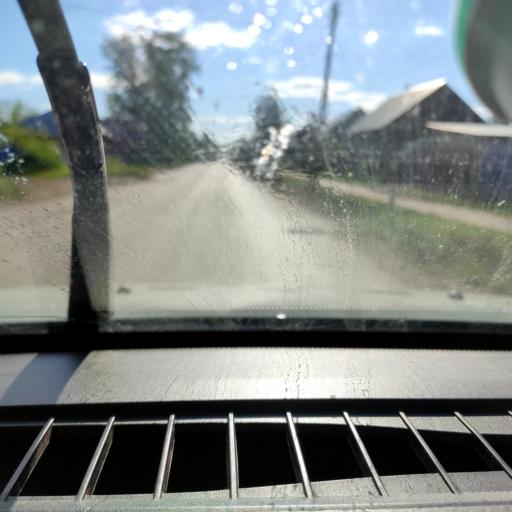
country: RU
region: Perm
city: Ocher
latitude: 57.8827
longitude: 54.7306
